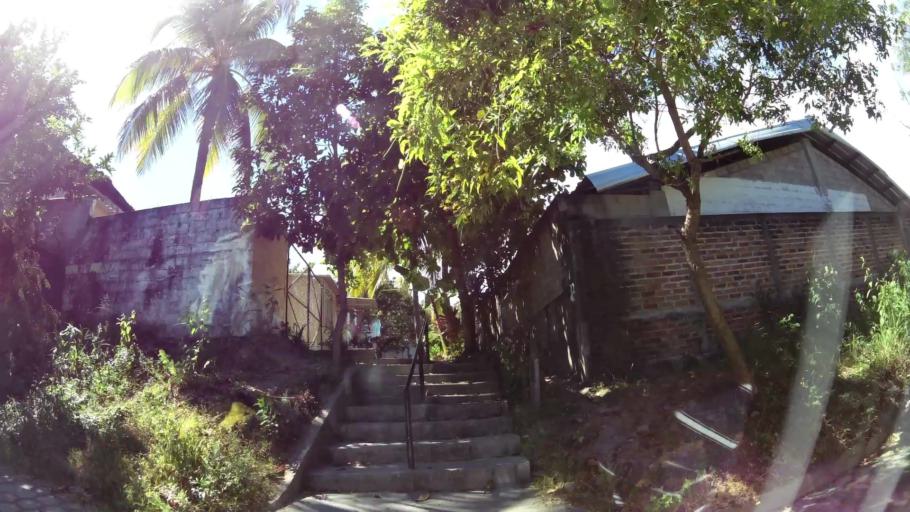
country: SV
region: San Salvador
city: Apopa
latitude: 13.8115
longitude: -89.1775
